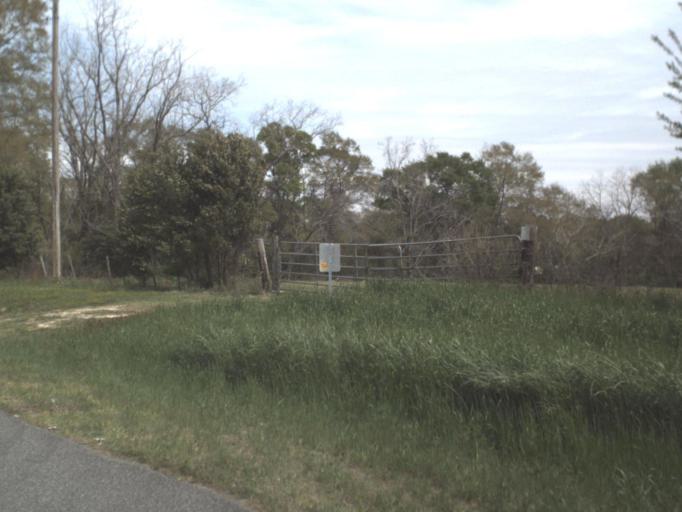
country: US
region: Florida
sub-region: Washington County
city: Chipley
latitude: 30.8355
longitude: -85.5026
